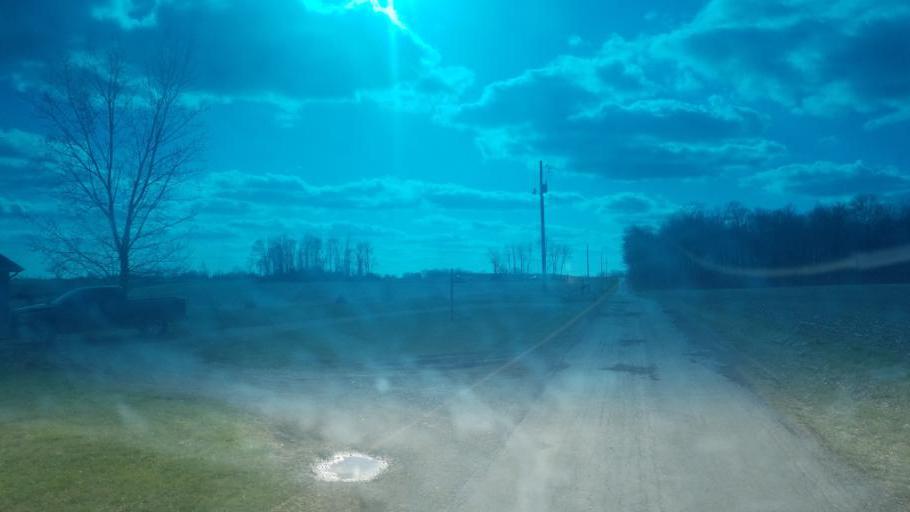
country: US
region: Ohio
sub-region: Highland County
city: Greenfield
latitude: 39.3172
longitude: -83.4150
